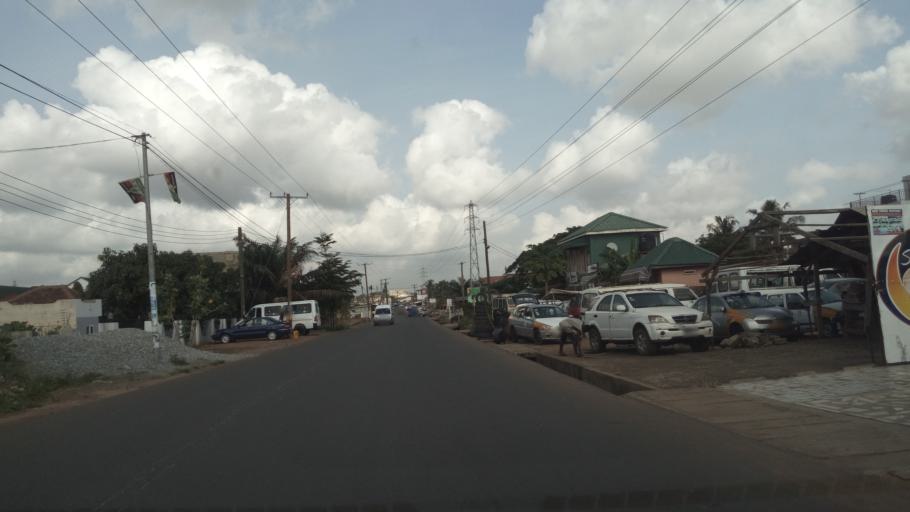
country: GH
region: Greater Accra
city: Medina Estates
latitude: 5.6599
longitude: -0.1532
